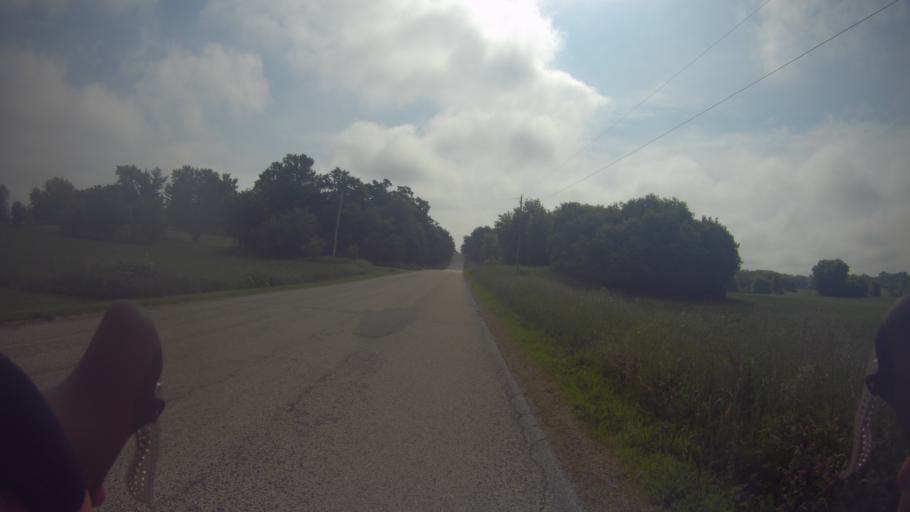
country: US
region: Wisconsin
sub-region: Dane County
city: Stoughton
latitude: 42.9410
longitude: -89.1786
